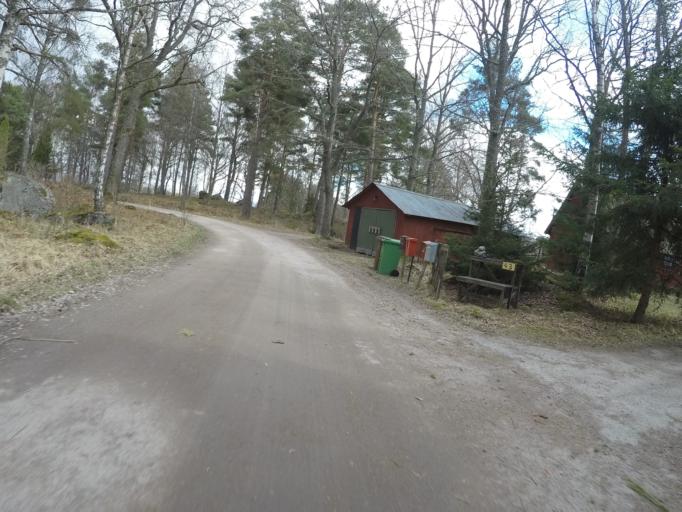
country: SE
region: Soedermanland
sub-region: Eskilstuna Kommun
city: Kvicksund
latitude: 59.4839
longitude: 16.2863
